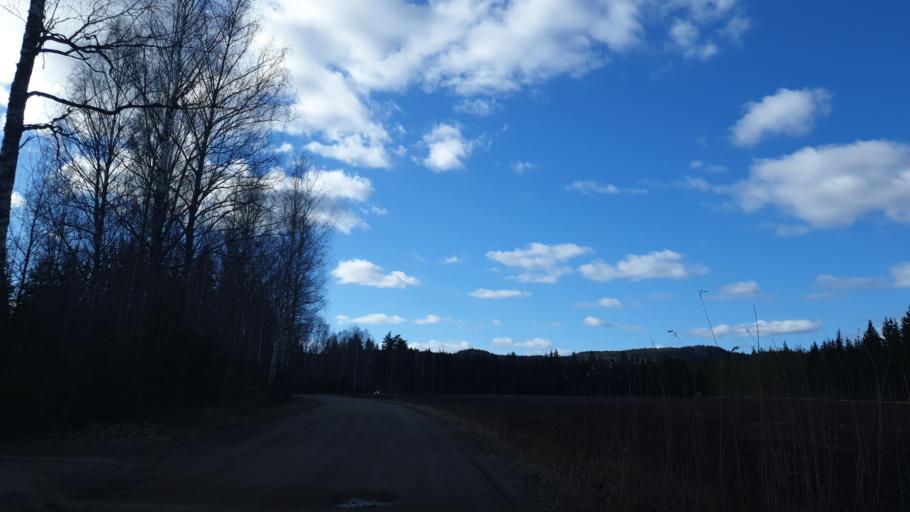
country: SE
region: OErebro
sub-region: Orebro Kommun
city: Garphyttan
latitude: 59.3482
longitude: 14.9974
